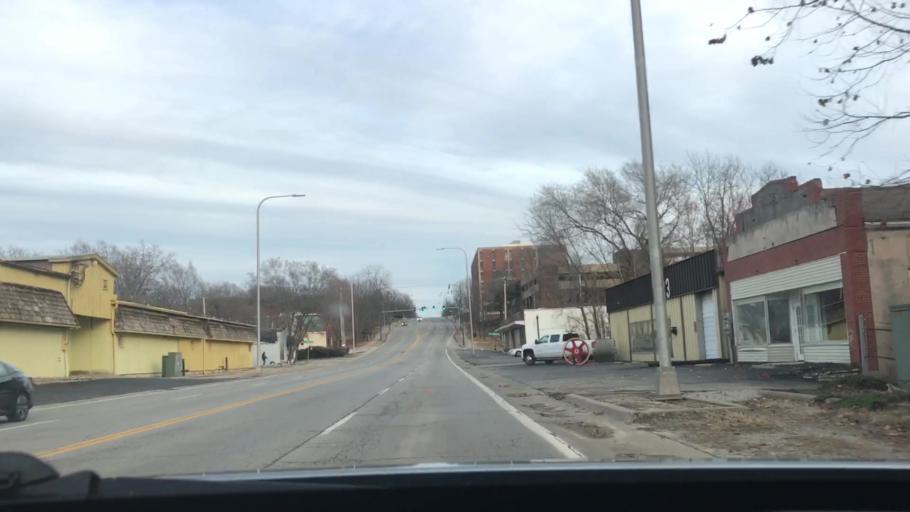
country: US
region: Missouri
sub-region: Jackson County
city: Sugar Creek
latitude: 39.0946
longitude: -94.4396
